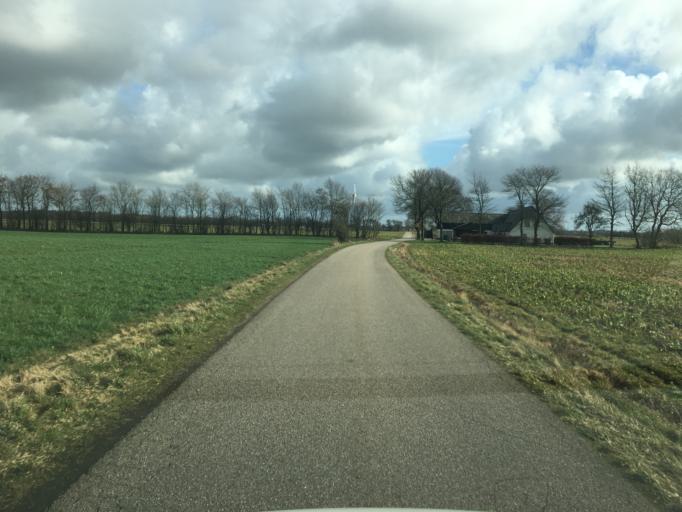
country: DK
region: South Denmark
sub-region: Aabenraa Kommune
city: Krusa
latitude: 54.9160
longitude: 9.3657
